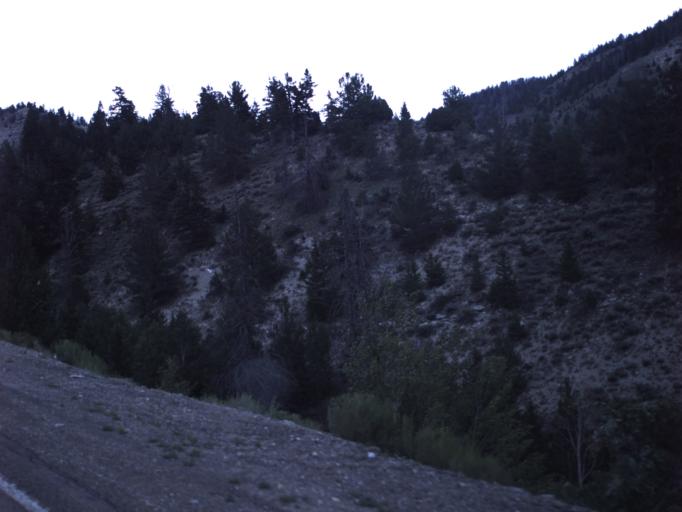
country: US
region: Utah
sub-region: Carbon County
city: Helper
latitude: 39.8592
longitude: -110.7652
